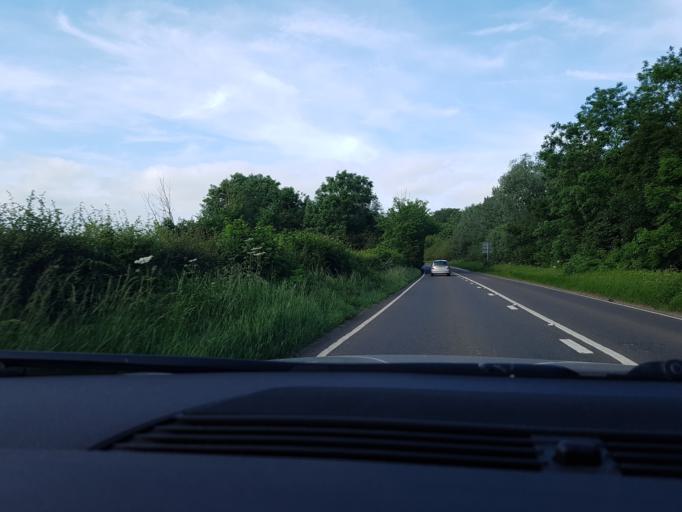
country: GB
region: England
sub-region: Northamptonshire
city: Deanshanger
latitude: 52.0223
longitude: -0.9158
